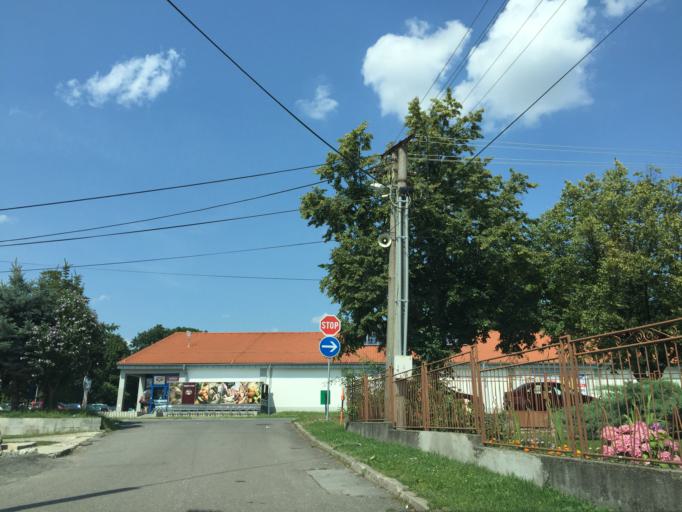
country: SK
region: Kosicky
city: Sobrance
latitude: 48.7441
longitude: 22.1833
